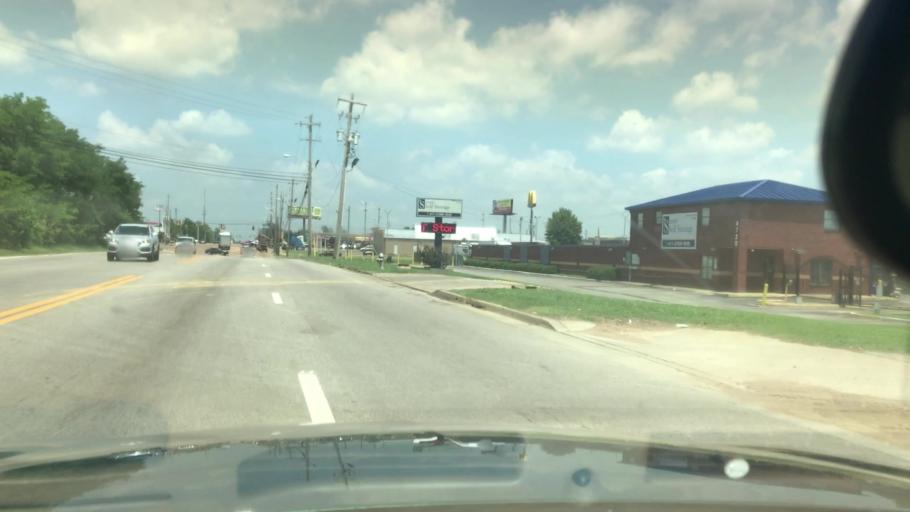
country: US
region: Mississippi
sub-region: De Soto County
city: Southaven
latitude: 35.0182
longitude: -89.9367
